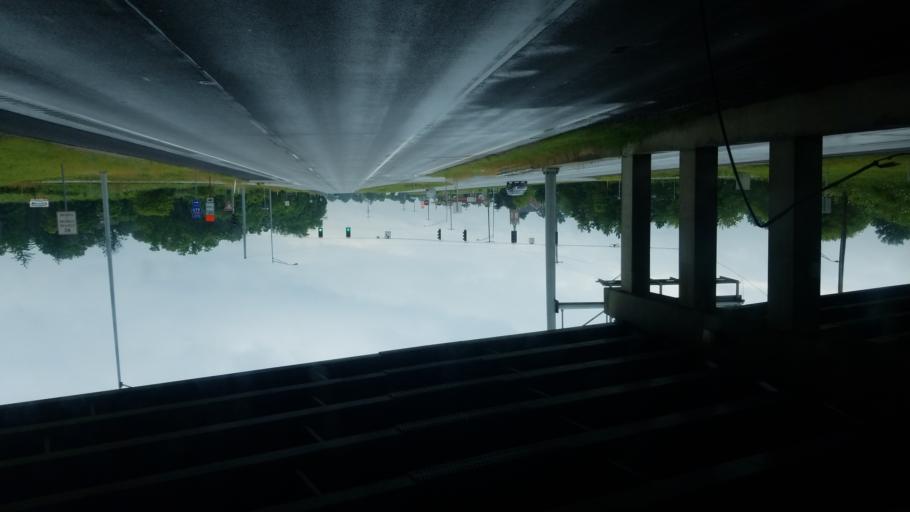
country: US
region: Indiana
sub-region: Allen County
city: New Haven
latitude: 40.9825
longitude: -85.0864
